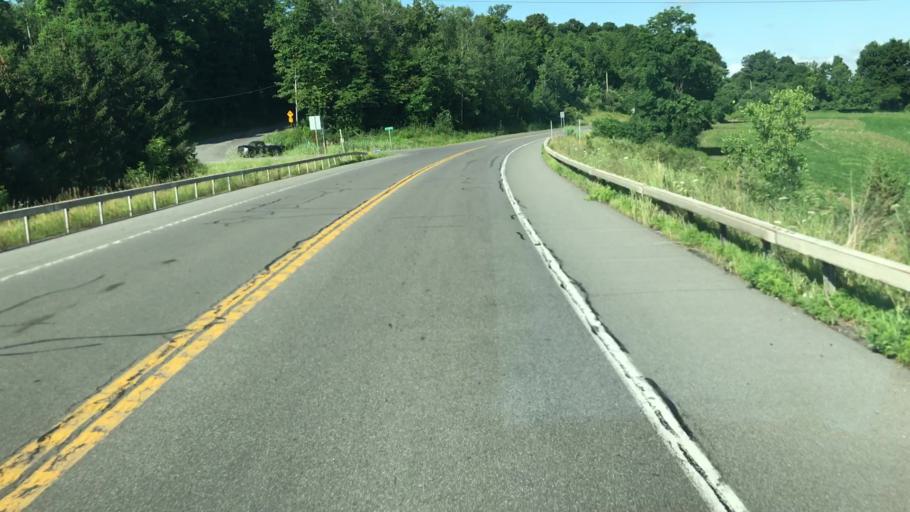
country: US
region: New York
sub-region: Onondaga County
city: Marcellus
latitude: 43.0216
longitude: -76.3645
